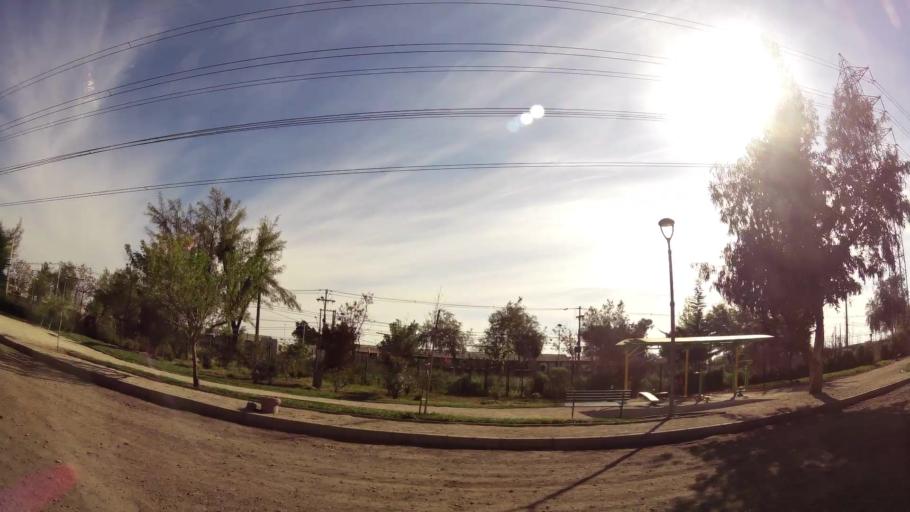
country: CL
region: Santiago Metropolitan
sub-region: Provincia de Santiago
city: Villa Presidente Frei, Nunoa, Santiago, Chile
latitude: -33.5141
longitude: -70.5593
